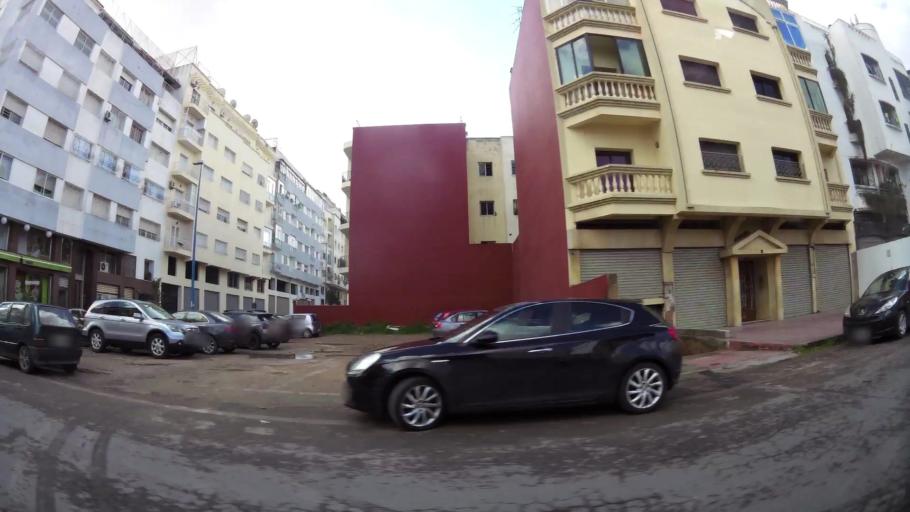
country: MA
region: Grand Casablanca
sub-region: Casablanca
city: Casablanca
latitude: 33.5550
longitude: -7.6245
